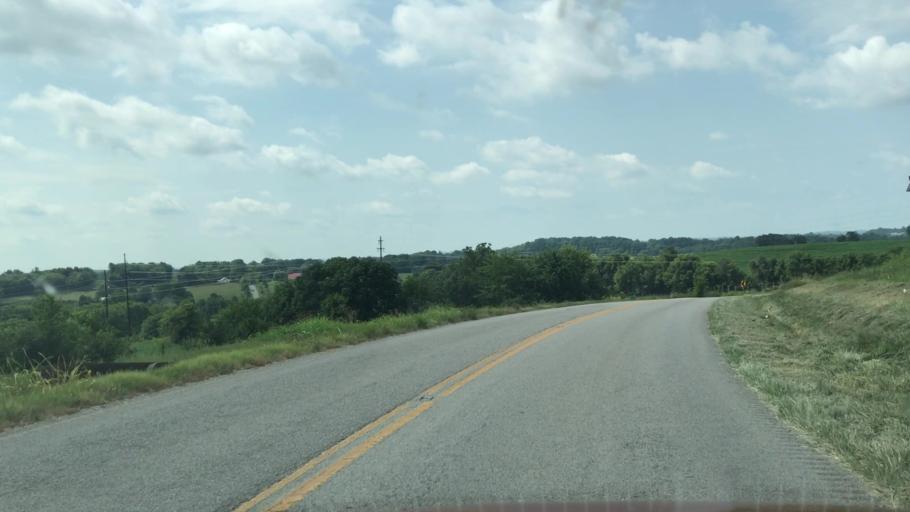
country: US
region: Kentucky
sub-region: Barren County
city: Glasgow
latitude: 36.9737
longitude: -85.8950
